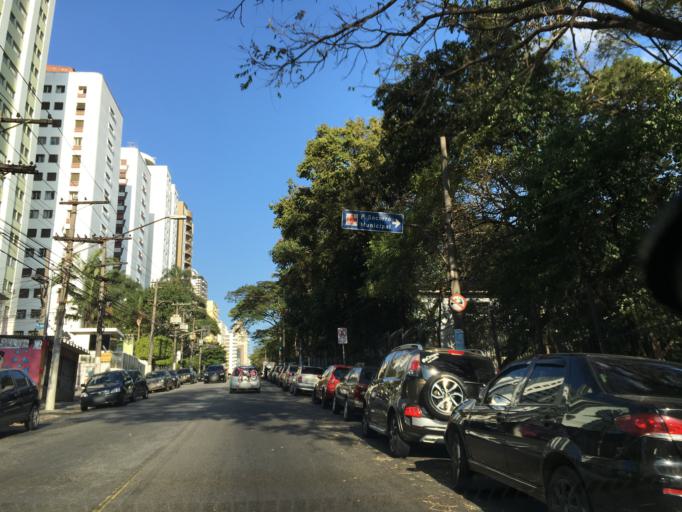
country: BR
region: Sao Paulo
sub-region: Sao Paulo
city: Sao Paulo
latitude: -23.4841
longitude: -46.6308
